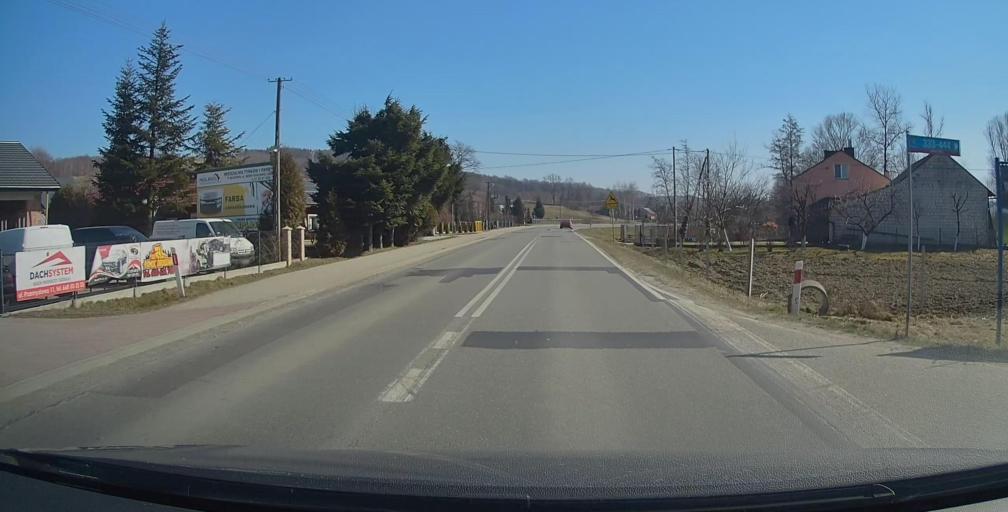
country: PL
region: Subcarpathian Voivodeship
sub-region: Powiat rzeszowski
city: Chmielnik
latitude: 49.9610
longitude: 22.0933
